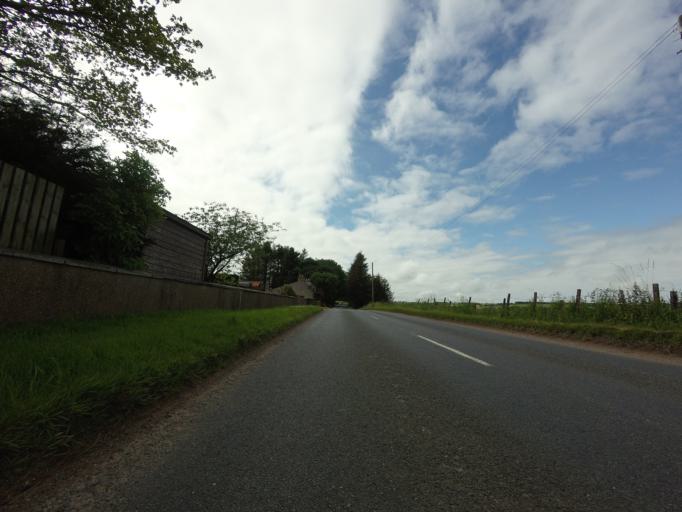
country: GB
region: Scotland
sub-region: Aberdeenshire
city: Turriff
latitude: 57.5426
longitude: -2.3134
